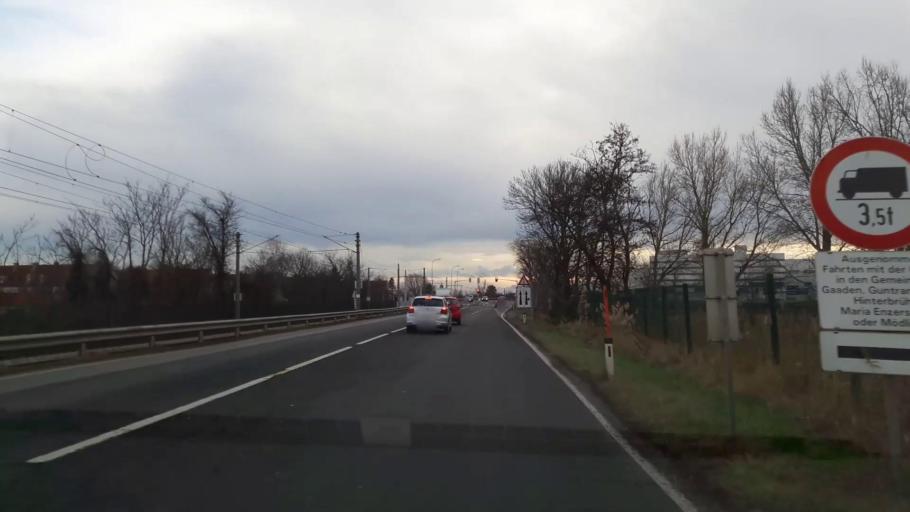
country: AT
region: Lower Austria
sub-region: Politischer Bezirk Modling
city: Neu-Guntramsdorf
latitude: 48.0657
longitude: 16.3131
